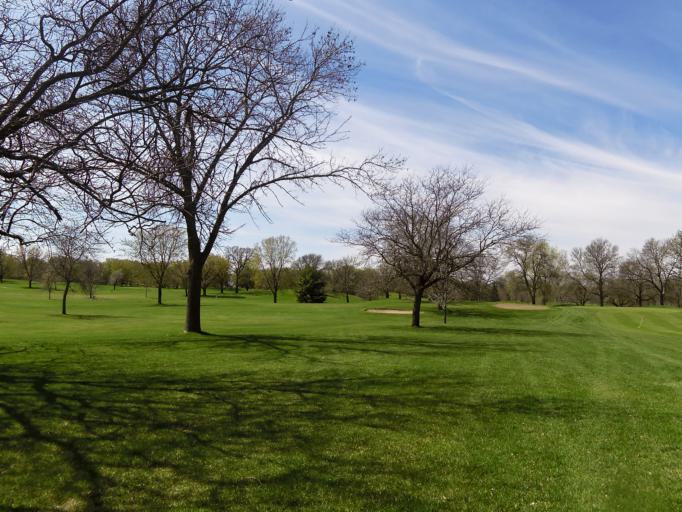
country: US
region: Minnesota
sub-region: Scott County
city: Savage
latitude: 44.8221
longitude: -93.3547
